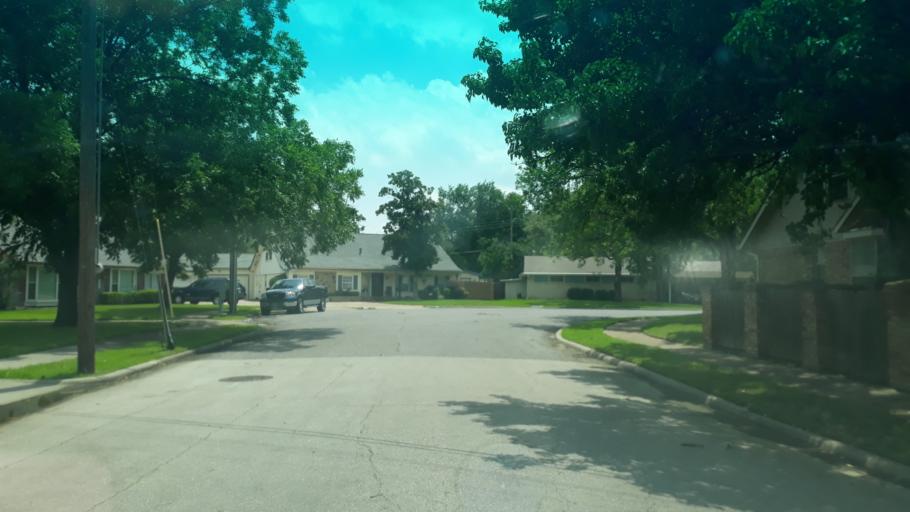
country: US
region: Texas
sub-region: Dallas County
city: Irving
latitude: 32.8546
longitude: -96.9621
